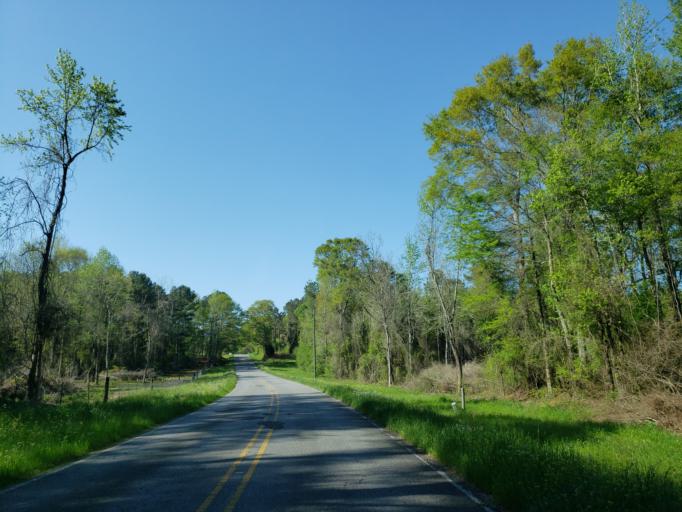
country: US
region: Mississippi
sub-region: Forrest County
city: Rawls Springs
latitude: 31.5306
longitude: -89.3596
